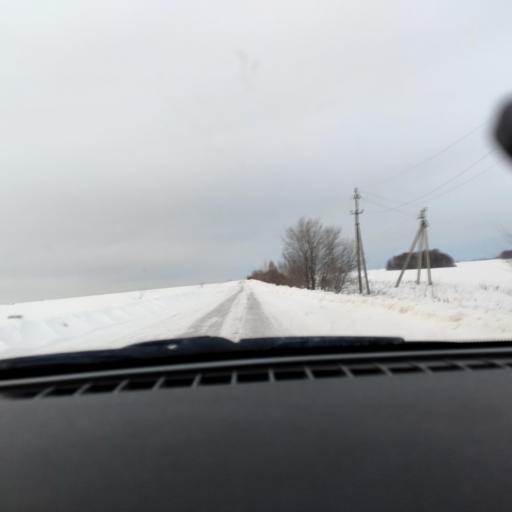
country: RU
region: Bashkortostan
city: Iglino
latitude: 54.7455
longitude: 56.5327
